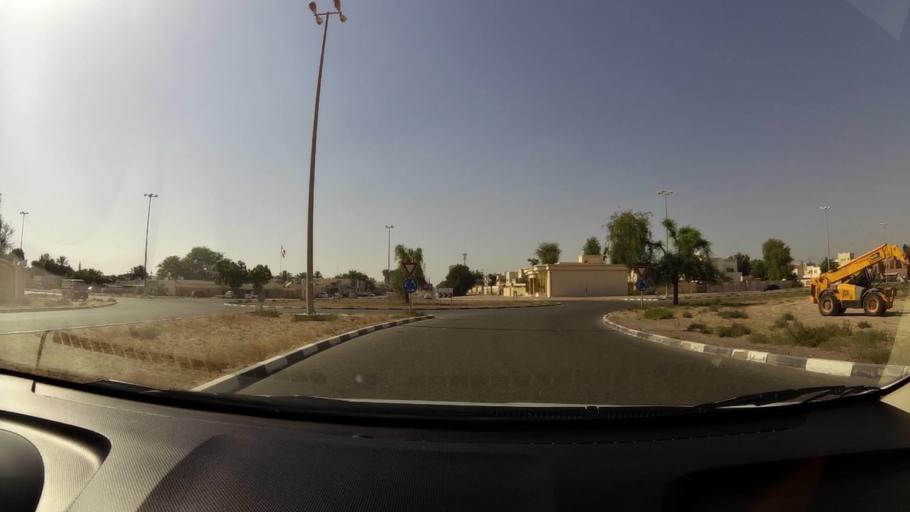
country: AE
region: Umm al Qaywayn
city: Umm al Qaywayn
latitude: 25.4952
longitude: 55.5811
